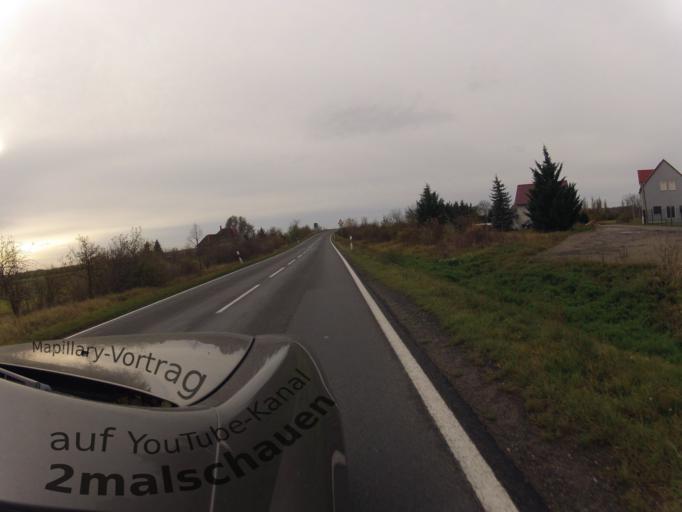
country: DE
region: Saxony-Anhalt
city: Beesenlaublingen
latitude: 51.7175
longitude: 11.7139
